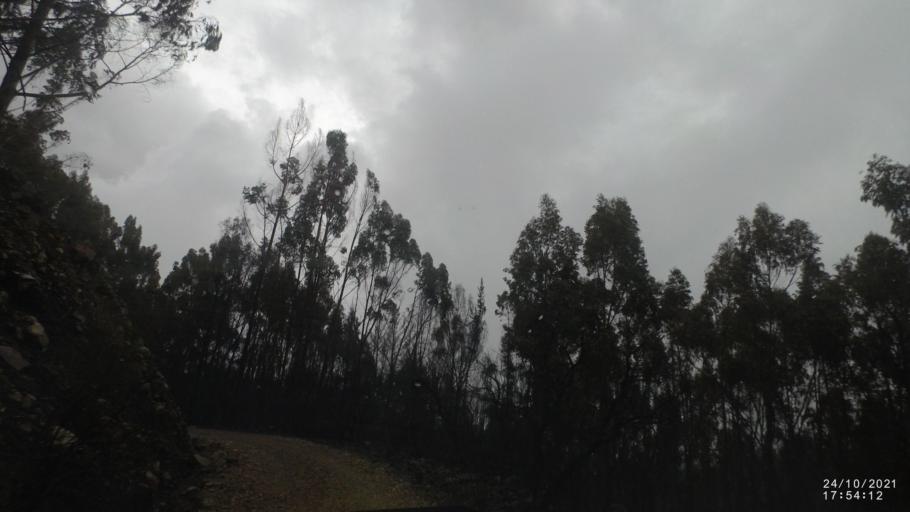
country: BO
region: Cochabamba
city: Cochabamba
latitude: -17.3201
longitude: -66.1304
